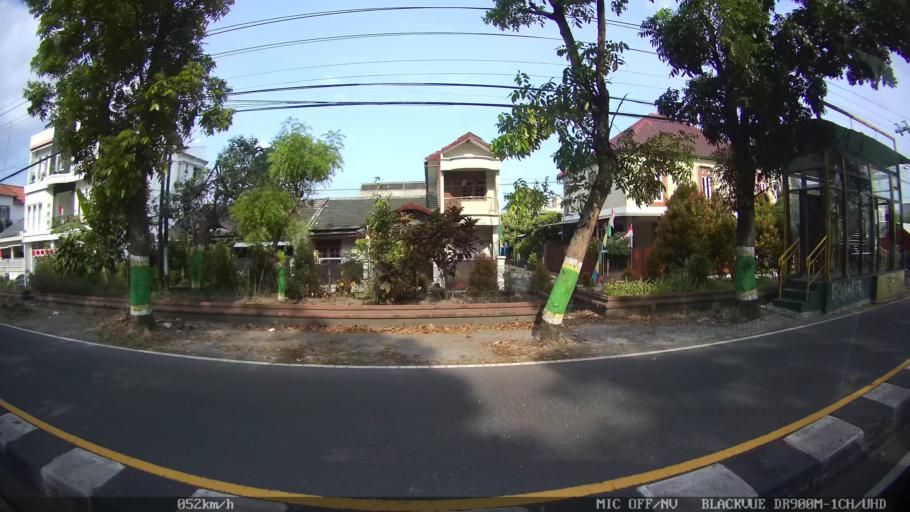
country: ID
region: Daerah Istimewa Yogyakarta
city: Yogyakarta
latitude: -7.7635
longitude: 110.3365
